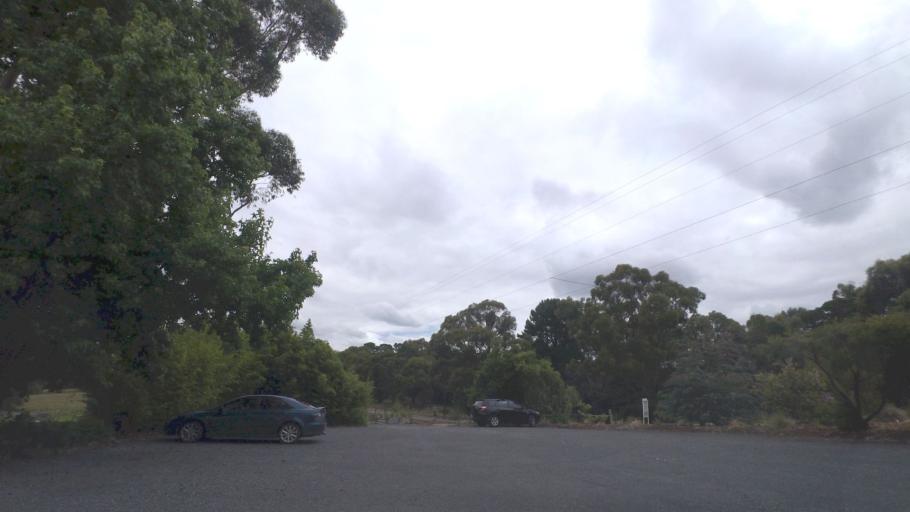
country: AU
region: Victoria
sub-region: Maroondah
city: Warranwood
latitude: -37.7630
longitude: 145.2439
